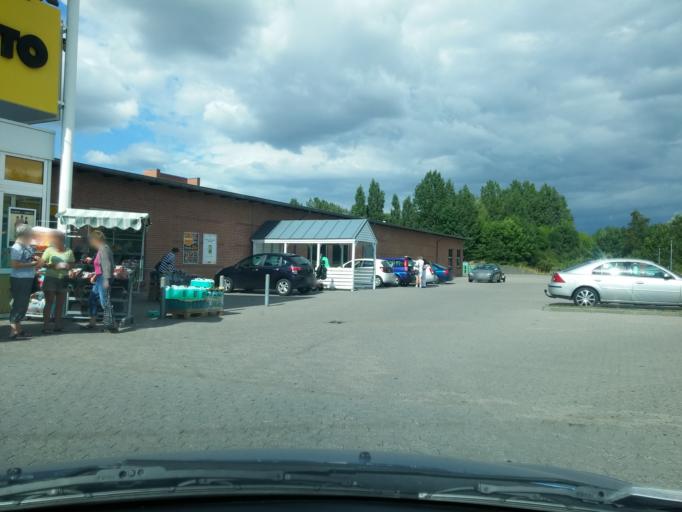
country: DK
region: South Denmark
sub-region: Odense Kommune
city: Seden
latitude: 55.4248
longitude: 10.4540
